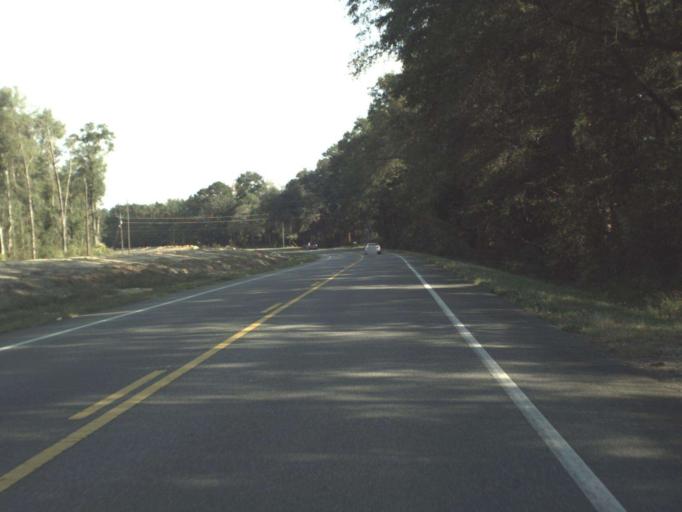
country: US
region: Florida
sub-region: Holmes County
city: Bonifay
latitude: 30.6469
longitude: -85.6993
